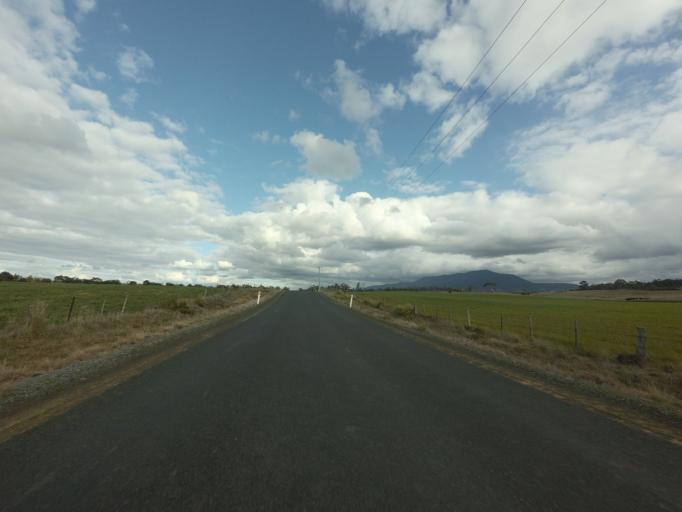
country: AU
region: Tasmania
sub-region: Northern Midlands
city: Longford
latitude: -41.8280
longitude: 147.2053
